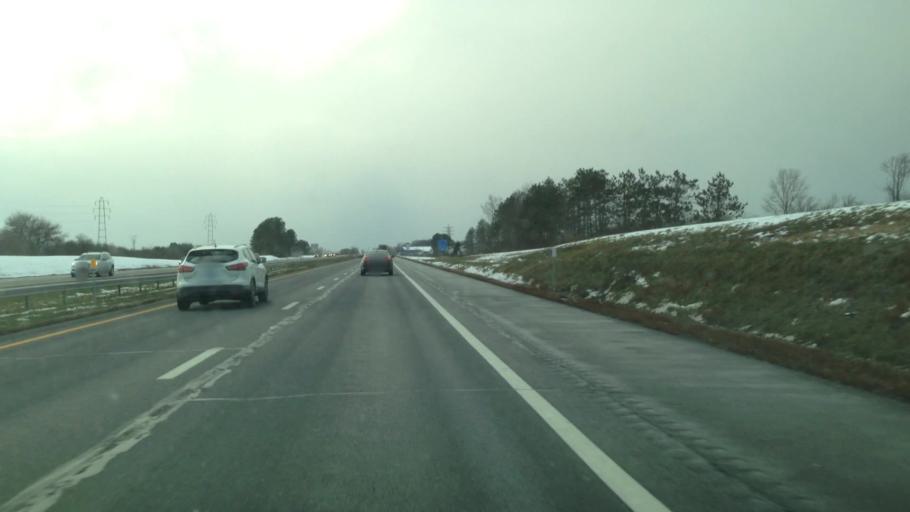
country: US
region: New York
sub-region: Montgomery County
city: Amsterdam
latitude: 42.9309
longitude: -74.2330
